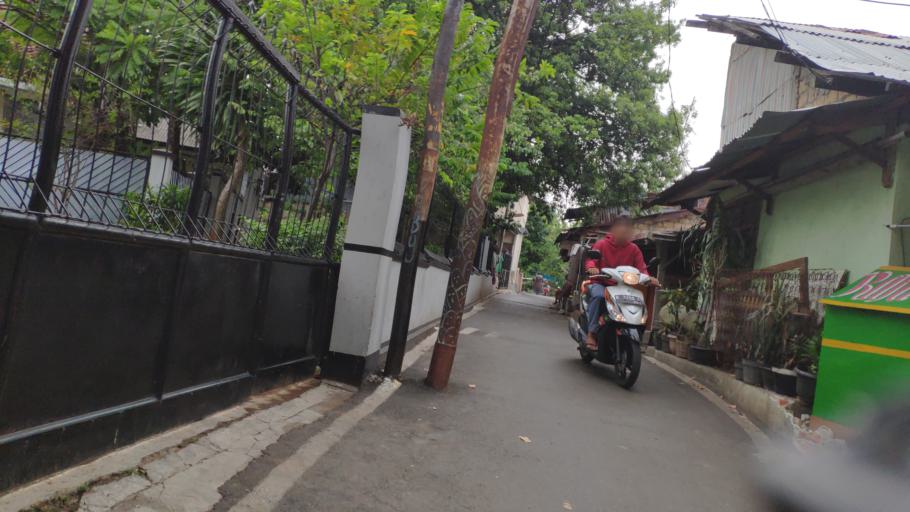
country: ID
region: West Java
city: Depok
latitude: -6.3369
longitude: 106.8337
